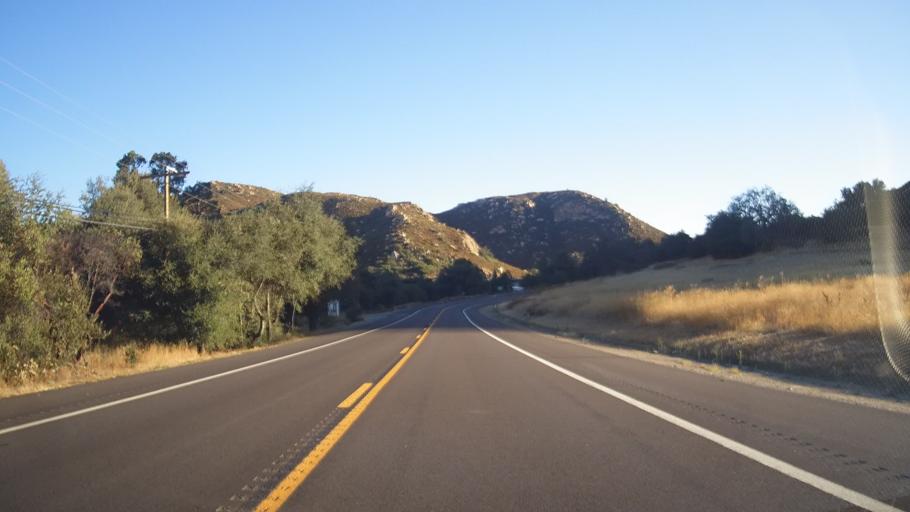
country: US
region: California
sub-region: San Diego County
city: Descanso
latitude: 32.8329
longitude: -116.6224
